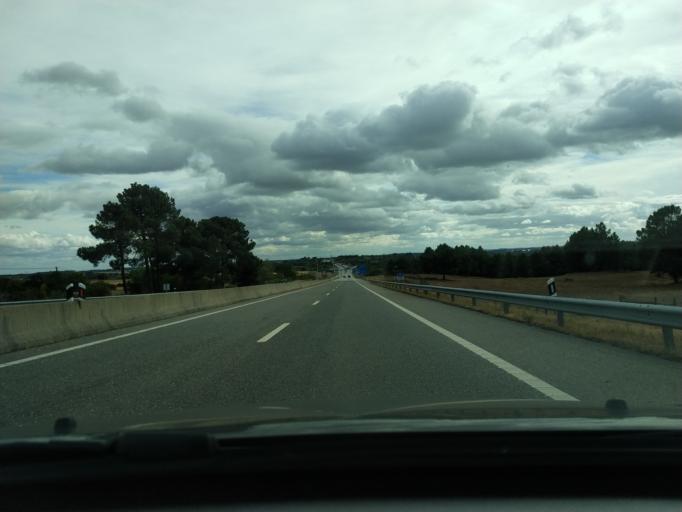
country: PT
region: Castelo Branco
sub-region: Concelho do Fundao
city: Fundao
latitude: 40.0408
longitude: -7.4699
